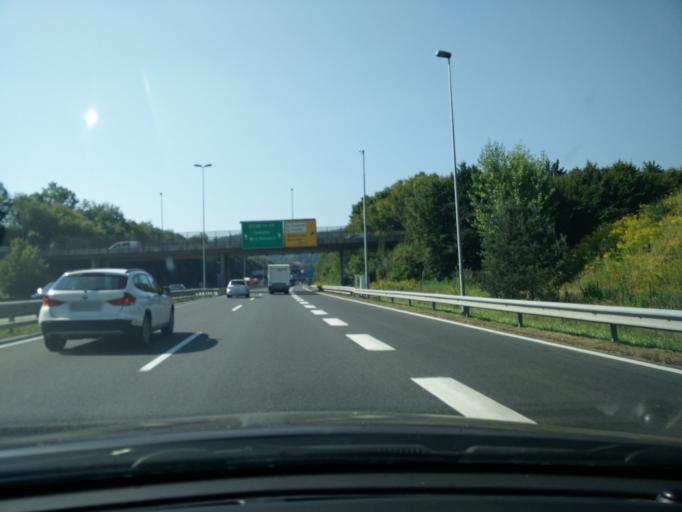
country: SI
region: Medvode
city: Zgornje Pirnice
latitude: 46.1054
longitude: 14.4695
